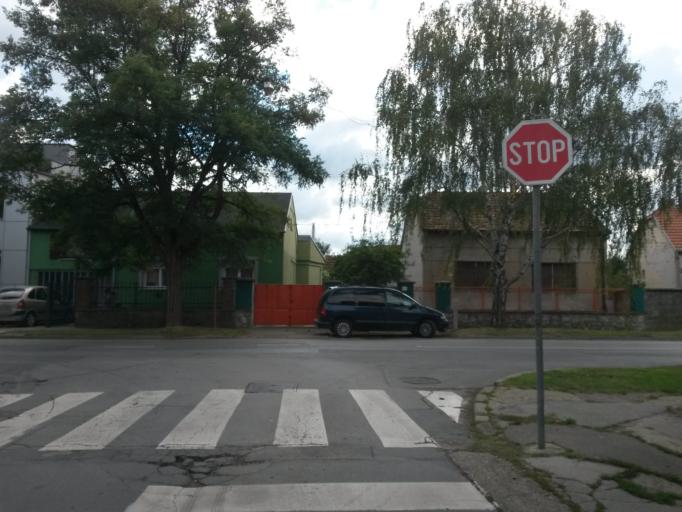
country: HR
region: Osjecko-Baranjska
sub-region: Grad Osijek
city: Osijek
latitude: 45.5570
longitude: 18.6586
